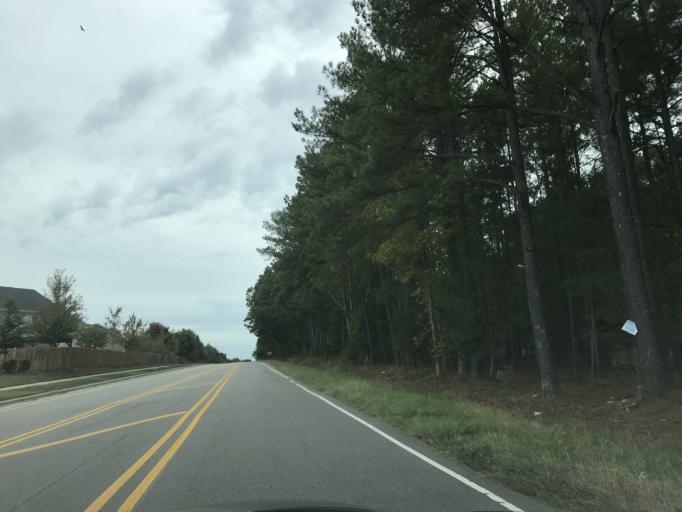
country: US
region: North Carolina
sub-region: Wake County
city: Knightdale
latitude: 35.8127
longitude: -78.4875
